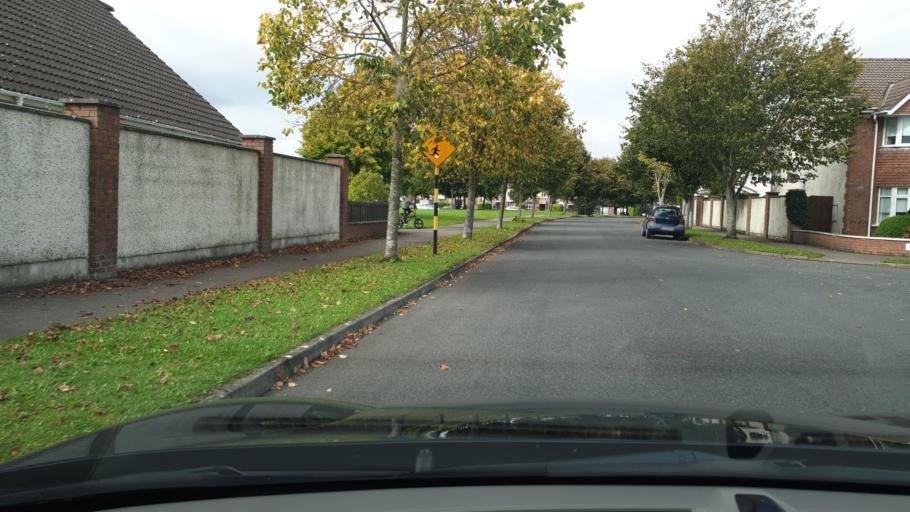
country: IE
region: Leinster
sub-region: Kildare
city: Sallins
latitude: 53.2347
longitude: -6.6542
